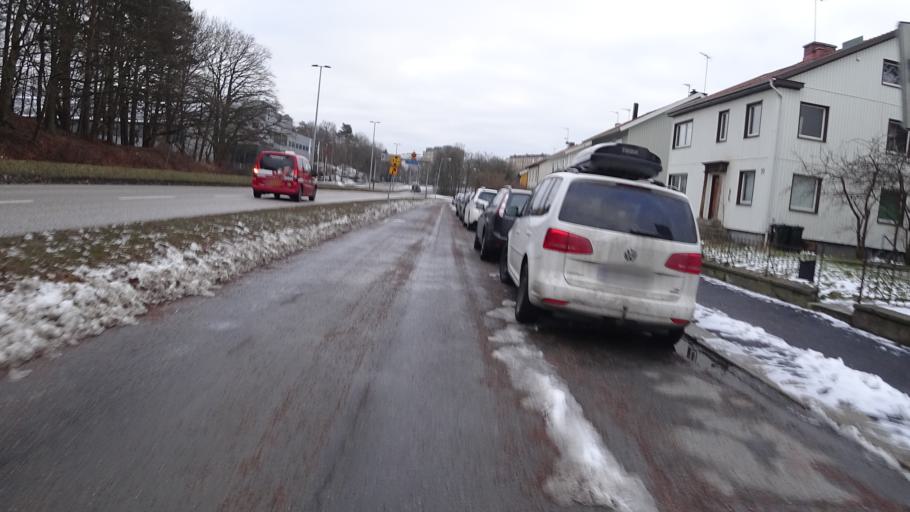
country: SE
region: Vaestra Goetaland
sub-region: Goteborg
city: Majorna
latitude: 57.6791
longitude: 11.9352
